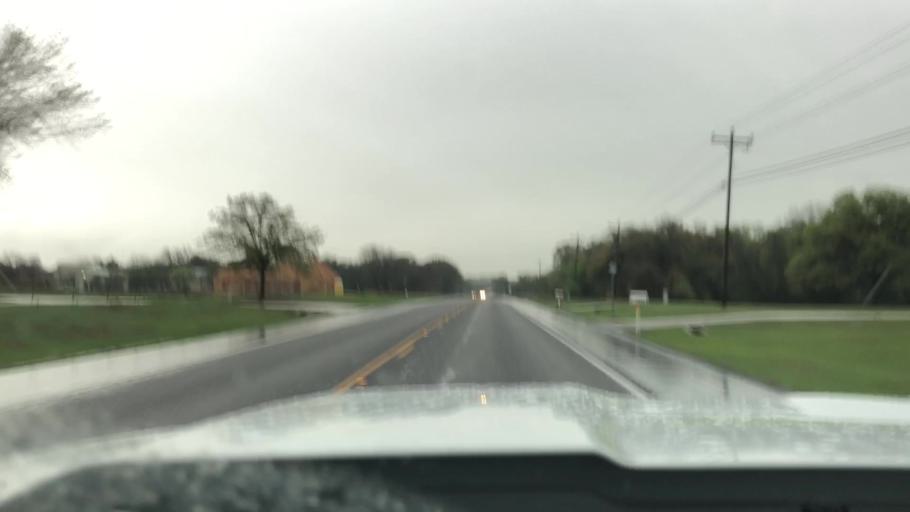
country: US
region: Texas
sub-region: Johnson County
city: Keene
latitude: 32.4304
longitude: -97.3155
